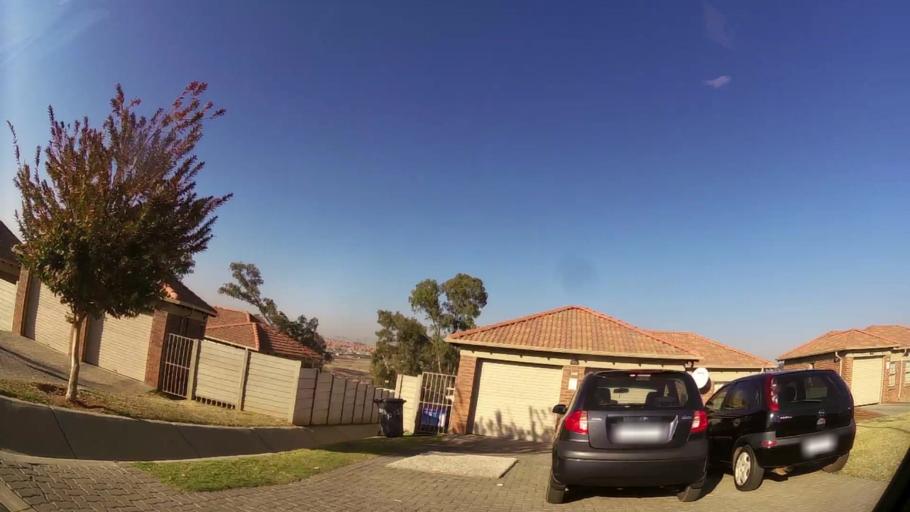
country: ZA
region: Gauteng
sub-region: City of Johannesburg Metropolitan Municipality
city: Midrand
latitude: -25.9089
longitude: 28.1065
